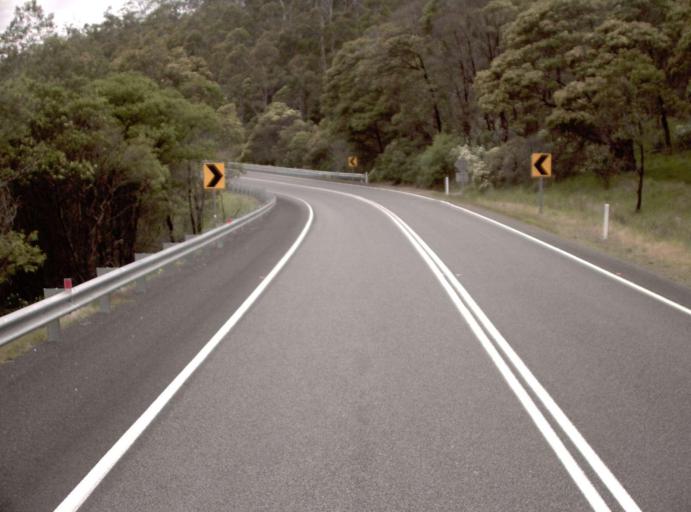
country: AU
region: New South Wales
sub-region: Bombala
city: Bombala
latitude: -37.2400
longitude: 149.2620
